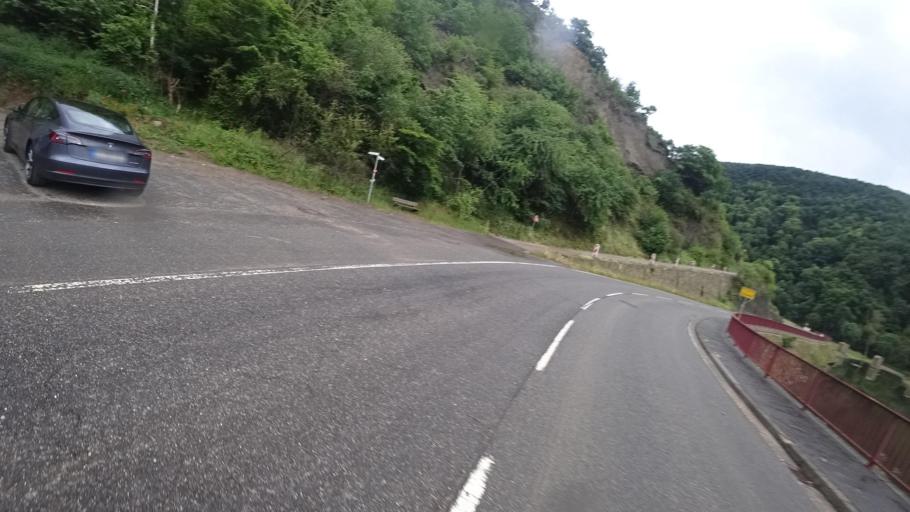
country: DE
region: Rheinland-Pfalz
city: Dernau
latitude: 50.5350
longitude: 7.0595
